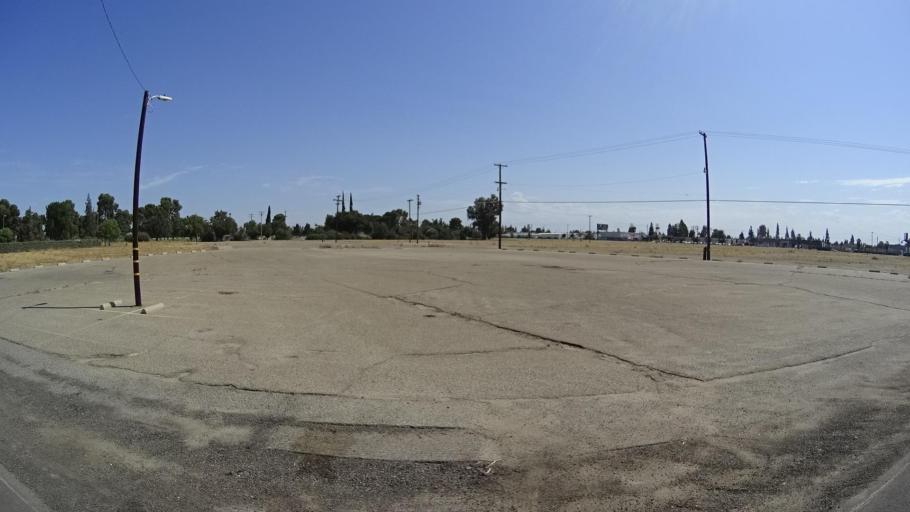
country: US
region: California
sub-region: Fresno County
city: Tarpey Village
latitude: 36.7740
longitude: -119.7039
